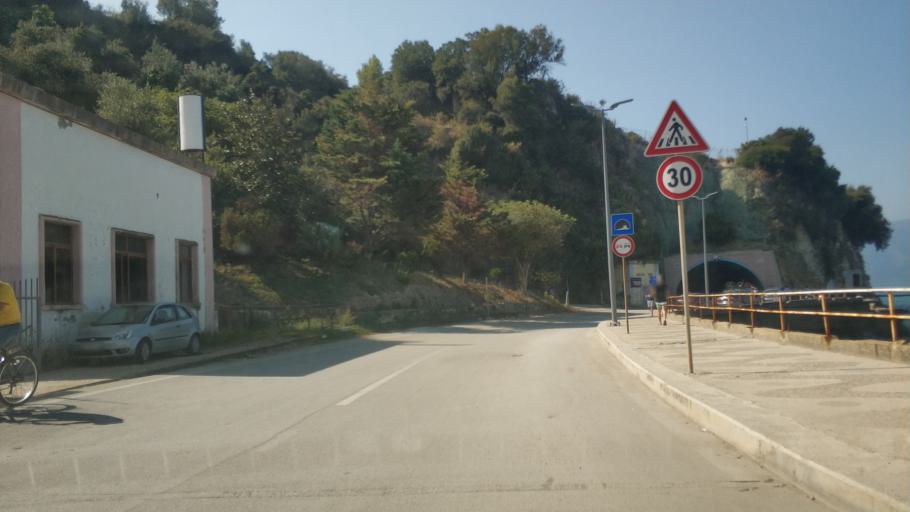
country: AL
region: Vlore
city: Vlore
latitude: 40.4218
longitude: 19.4887
